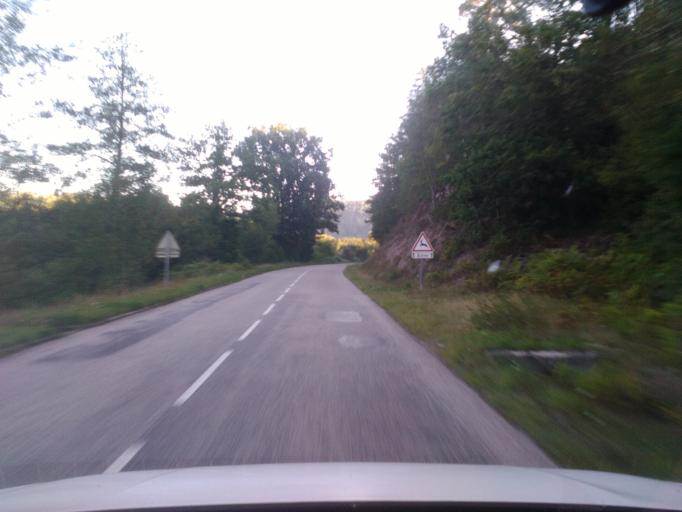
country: FR
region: Lorraine
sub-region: Departement des Vosges
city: Taintrux
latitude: 48.2267
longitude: 6.9045
